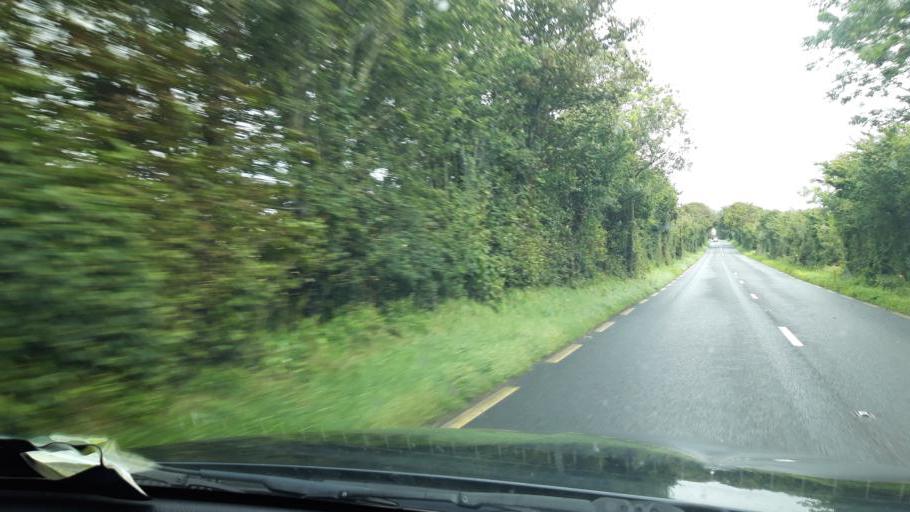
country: IE
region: Leinster
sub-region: Loch Garman
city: New Ross
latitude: 52.4332
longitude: -6.7821
